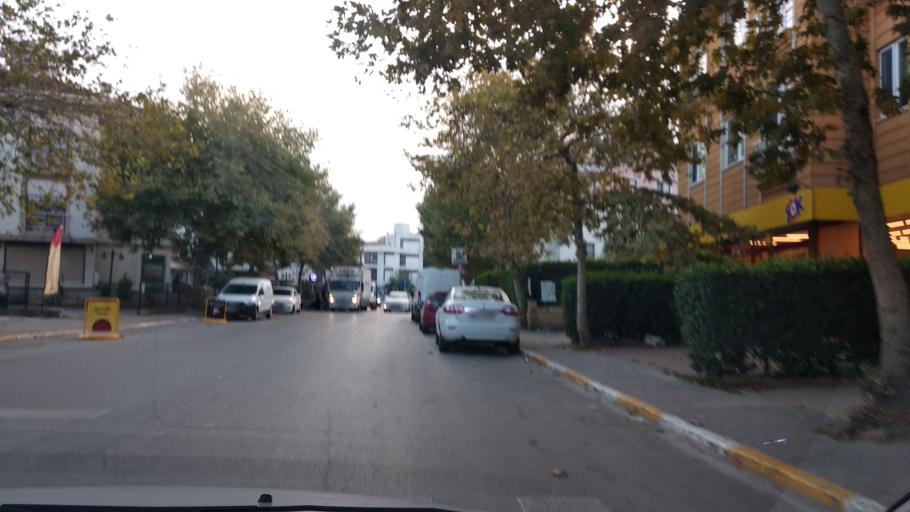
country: TR
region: Istanbul
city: Icmeler
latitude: 40.8199
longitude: 29.2991
